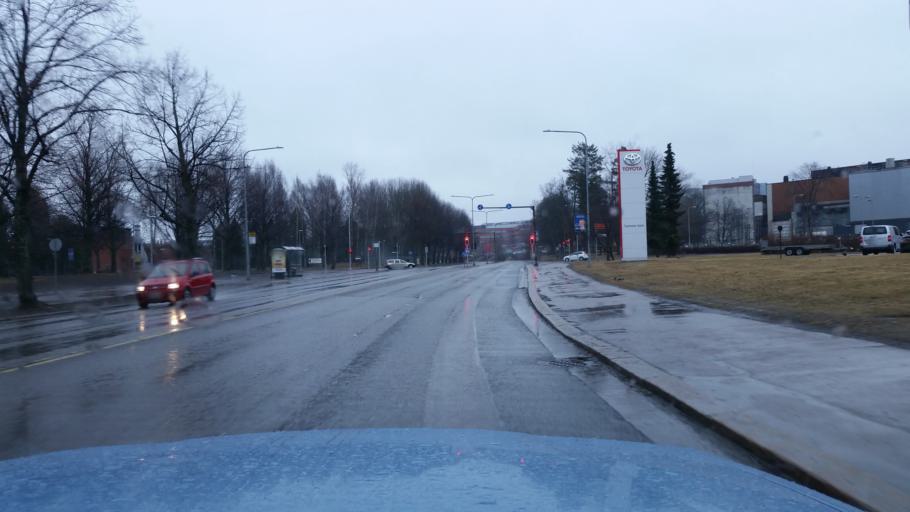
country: FI
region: Pirkanmaa
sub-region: Tampere
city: Tampere
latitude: 61.4856
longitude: 23.7640
